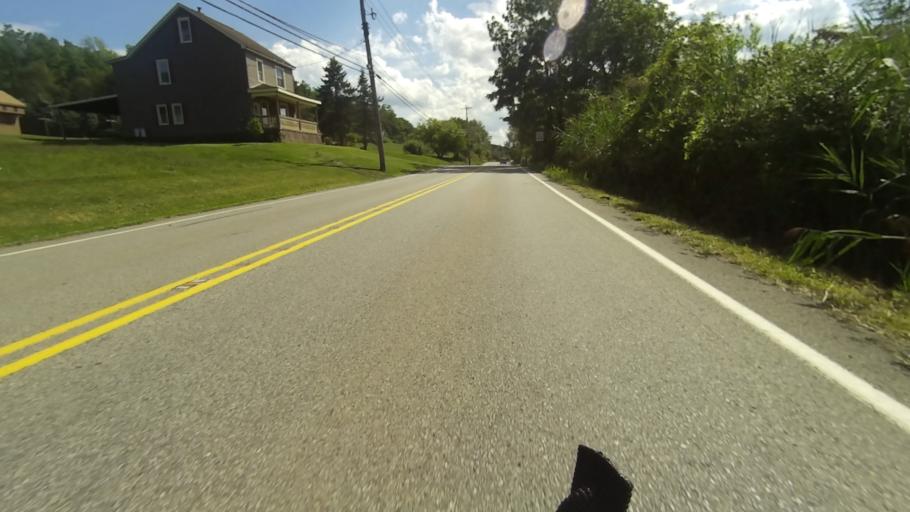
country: US
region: Pennsylvania
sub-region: Blair County
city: Greenwood
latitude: 40.5666
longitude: -78.3536
